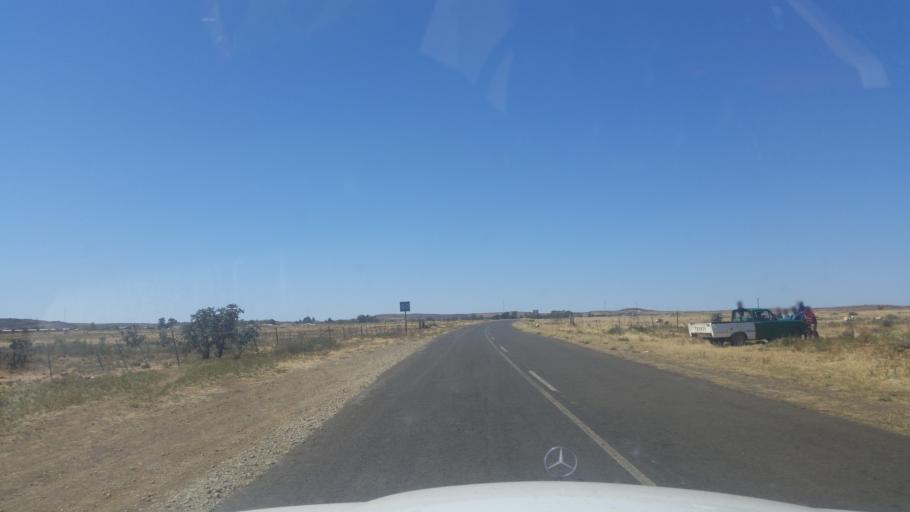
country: ZA
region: Eastern Cape
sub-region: Joe Gqabi District Municipality
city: Burgersdorp
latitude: -30.7624
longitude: 25.7844
